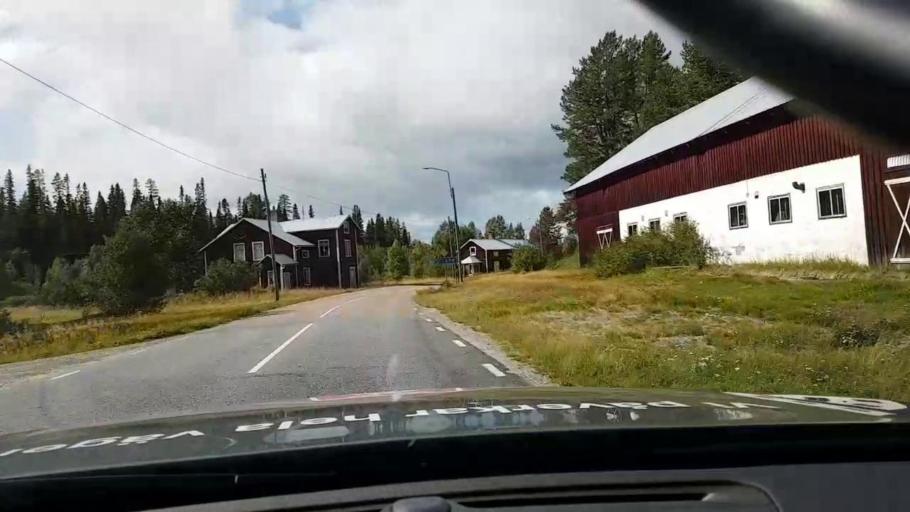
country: SE
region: Vaesterbotten
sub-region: Asele Kommun
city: Asele
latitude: 63.8604
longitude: 17.3749
